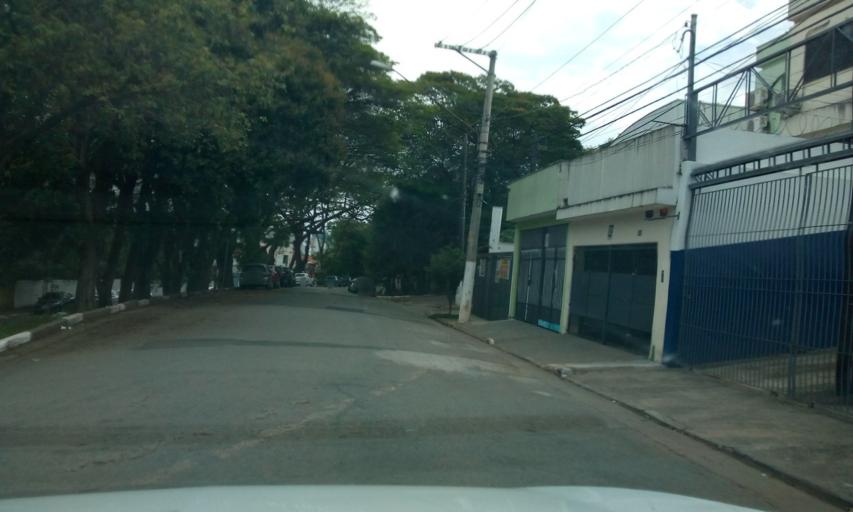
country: BR
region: Sao Paulo
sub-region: Diadema
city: Diadema
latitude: -23.6253
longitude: -46.6633
